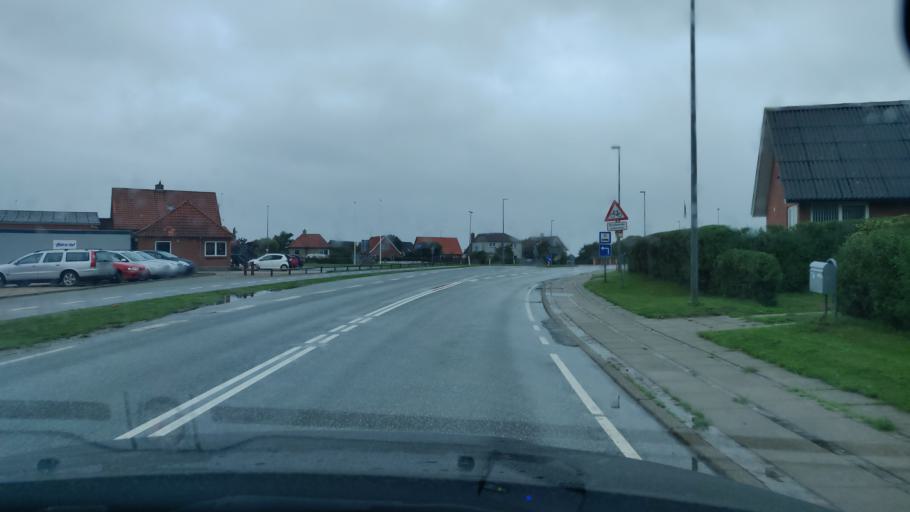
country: DK
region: North Denmark
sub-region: Thisted Kommune
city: Thisted
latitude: 56.8822
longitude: 8.6240
